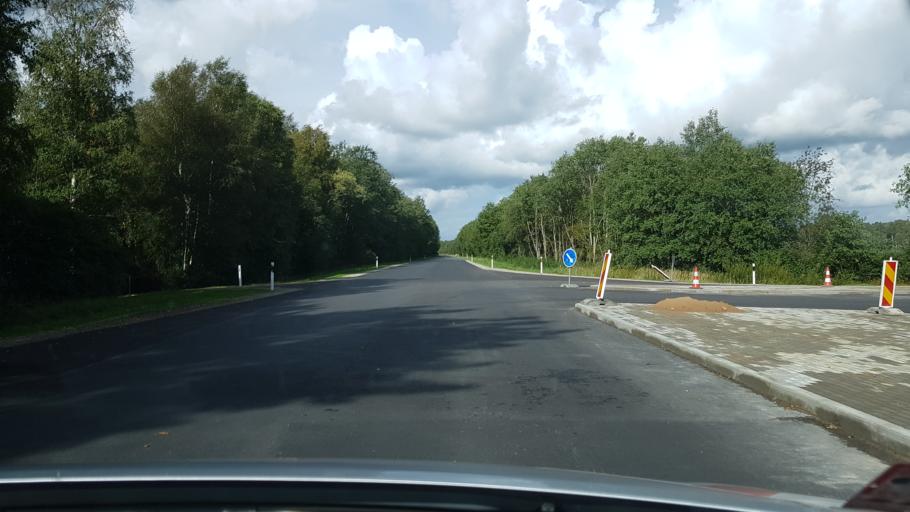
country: EE
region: Saare
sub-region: Kuressaare linn
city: Kuressaare
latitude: 58.2921
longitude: 22.3800
